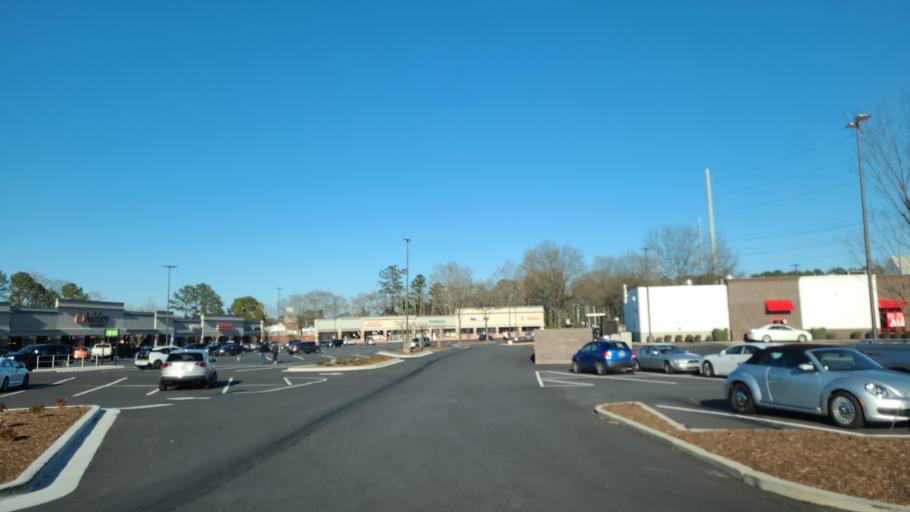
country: US
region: Georgia
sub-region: Fulton County
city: Roswell
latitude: 33.9856
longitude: -84.4258
